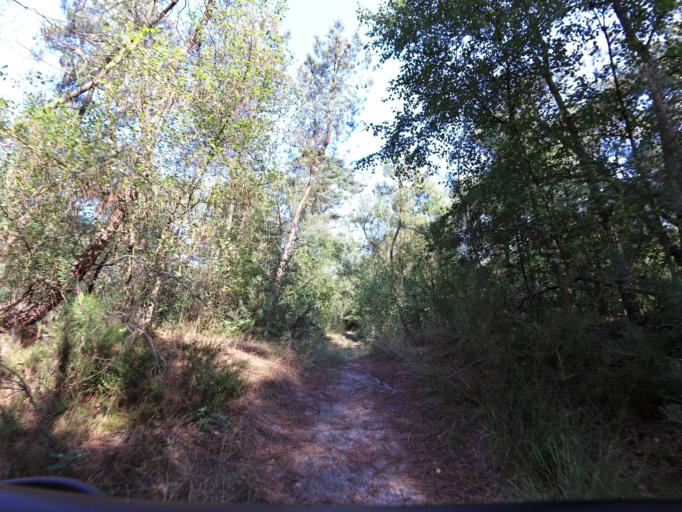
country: BE
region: Flanders
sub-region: Provincie Antwerpen
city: Stabroek
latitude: 51.3657
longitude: 4.3458
